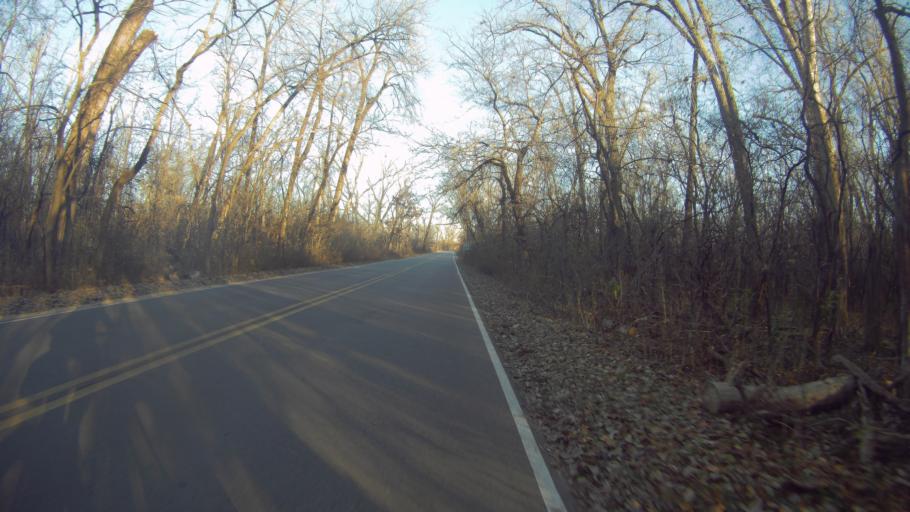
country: US
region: Wisconsin
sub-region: Dane County
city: Madison
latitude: 43.0497
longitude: -89.4147
